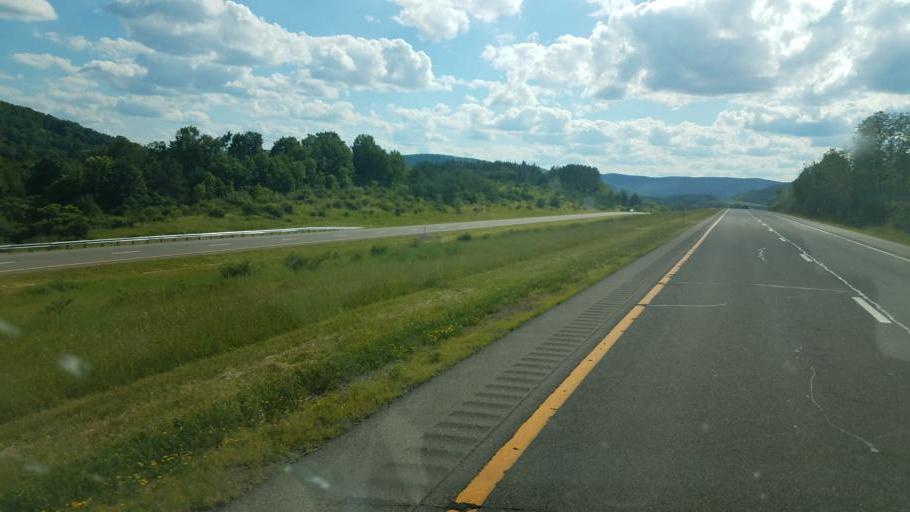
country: US
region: New York
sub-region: Allegany County
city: Cuba
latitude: 42.2263
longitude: -78.2567
